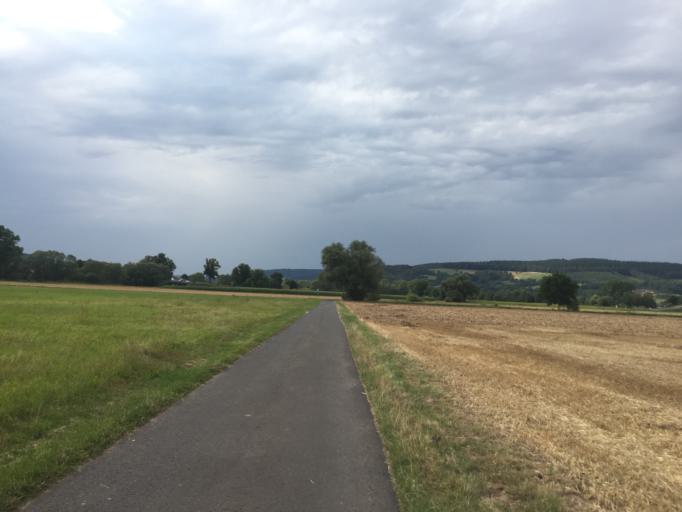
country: DE
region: Hesse
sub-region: Regierungsbezirk Kassel
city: Alheim
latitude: 51.0402
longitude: 9.6640
